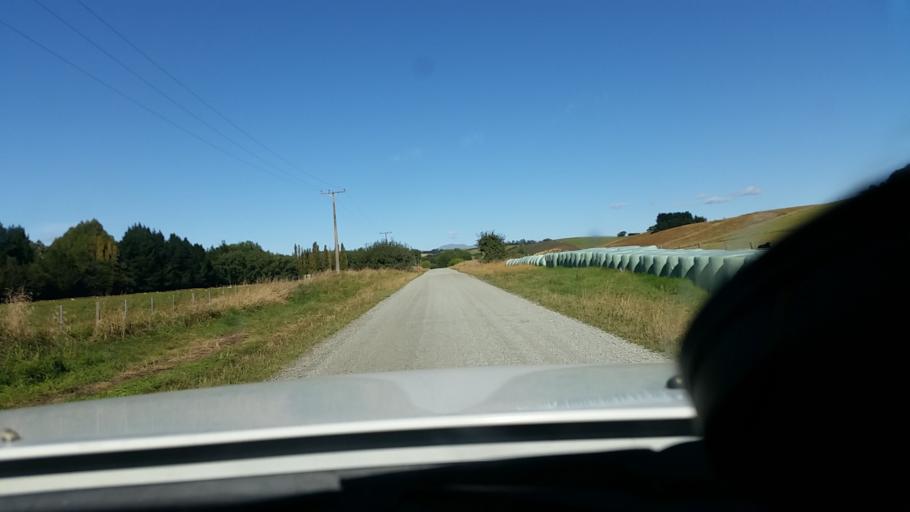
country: NZ
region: Canterbury
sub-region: Timaru District
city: Pleasant Point
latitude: -44.3385
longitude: 171.1767
